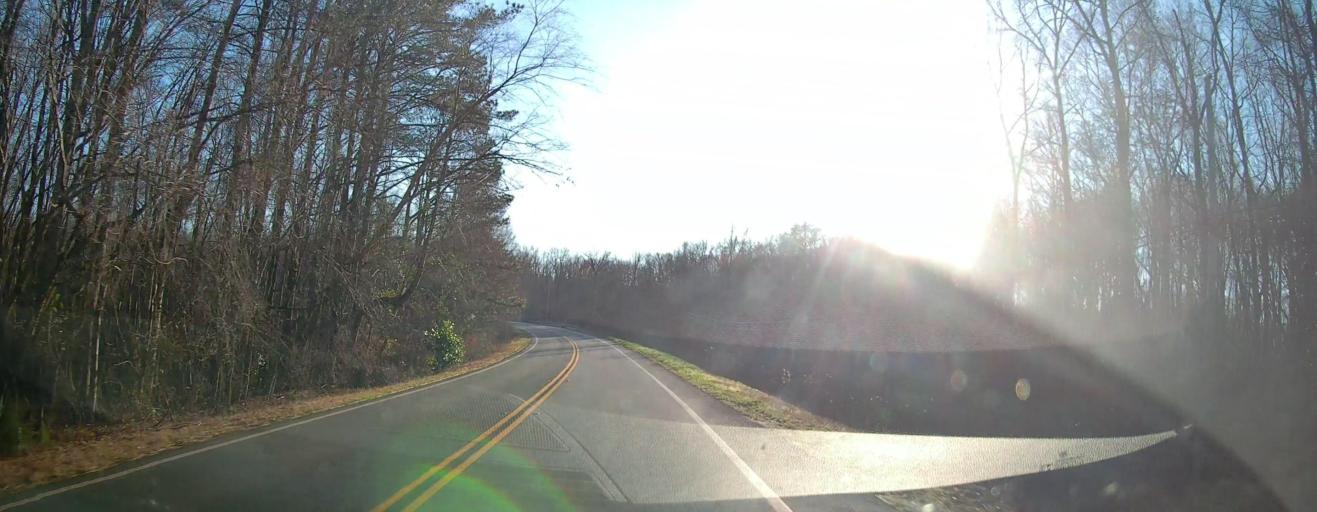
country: US
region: Georgia
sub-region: Harris County
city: Pine Mountain
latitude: 32.9150
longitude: -84.7993
